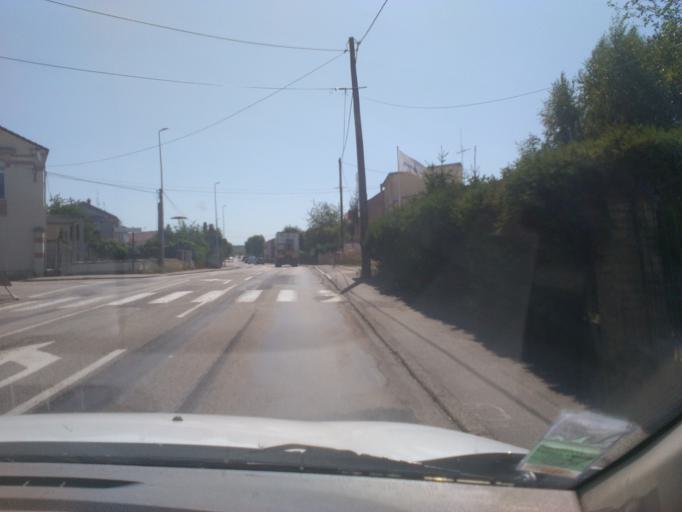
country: FR
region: Lorraine
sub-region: Departement des Vosges
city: Rambervillers
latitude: 48.3345
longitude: 6.6360
